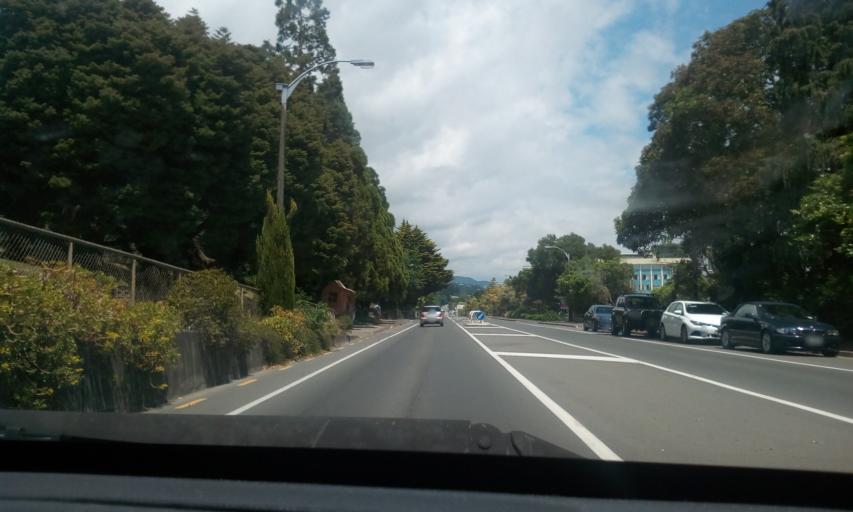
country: NZ
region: Nelson
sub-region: Nelson City
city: Nelson
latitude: -41.2859
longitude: 173.2750
